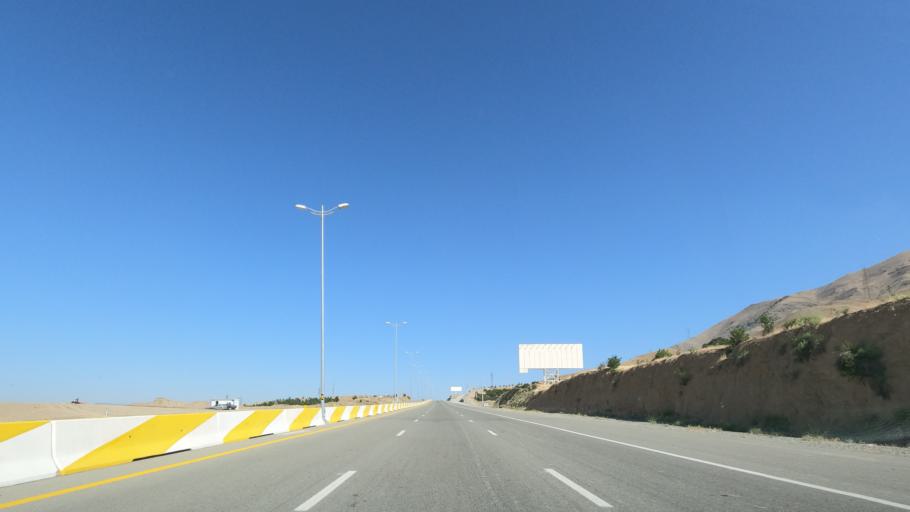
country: IR
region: Tehran
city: Shahr-e Qods
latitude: 35.7628
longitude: 51.0727
